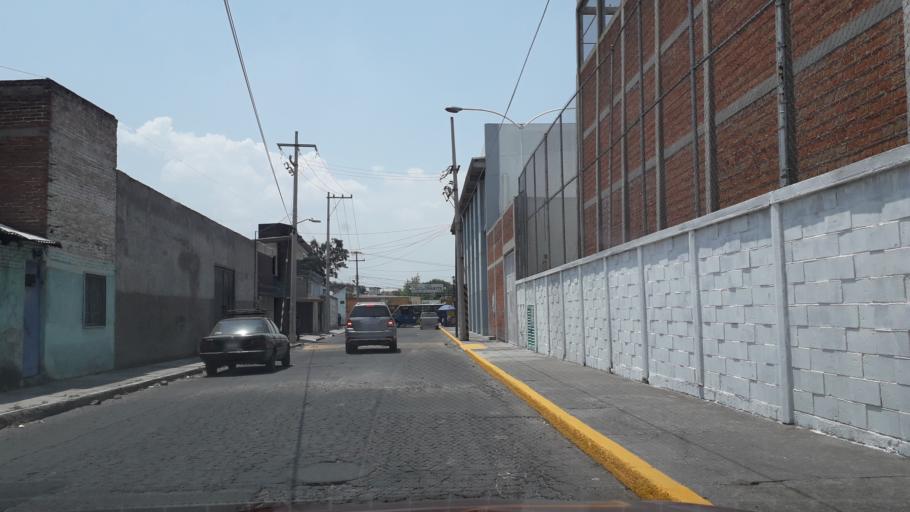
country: MX
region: Puebla
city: Puebla
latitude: 19.0469
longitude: -98.1700
